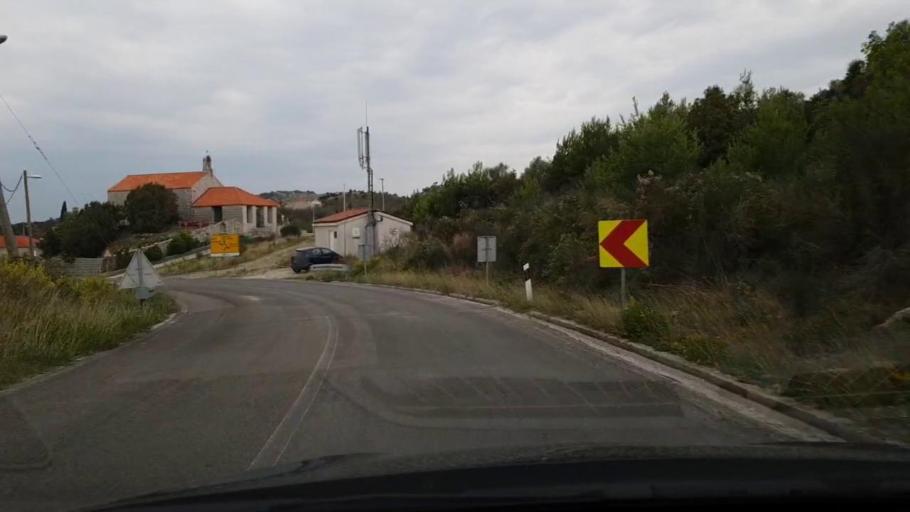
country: HR
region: Dubrovacko-Neretvanska
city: Cibaca
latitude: 42.6465
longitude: 18.1586
